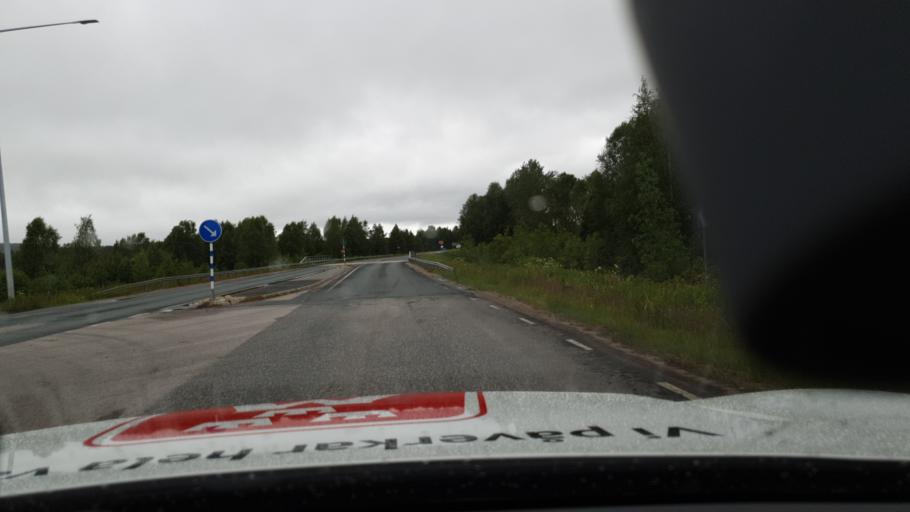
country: SE
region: Norrbotten
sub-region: Overtornea Kommun
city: OEvertornea
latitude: 66.3966
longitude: 23.6257
